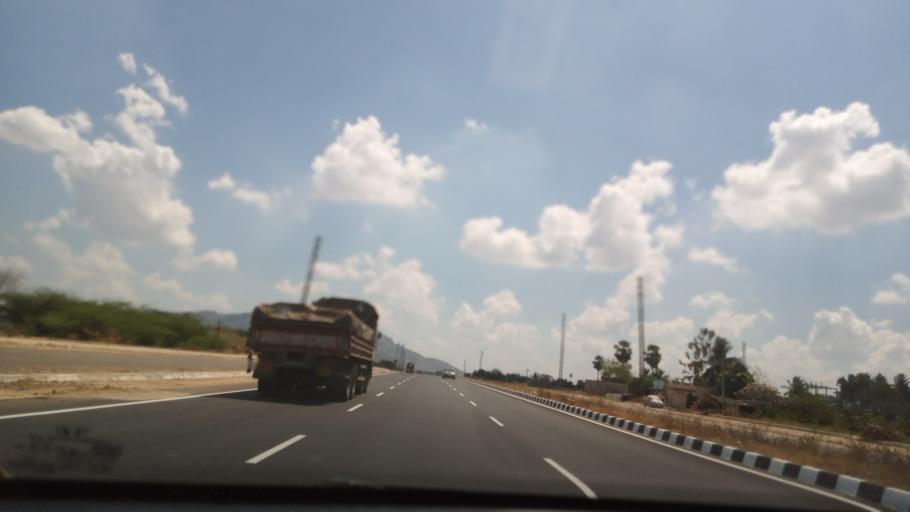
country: IN
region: Andhra Pradesh
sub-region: Chittoor
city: Pakala
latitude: 13.3620
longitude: 79.0880
